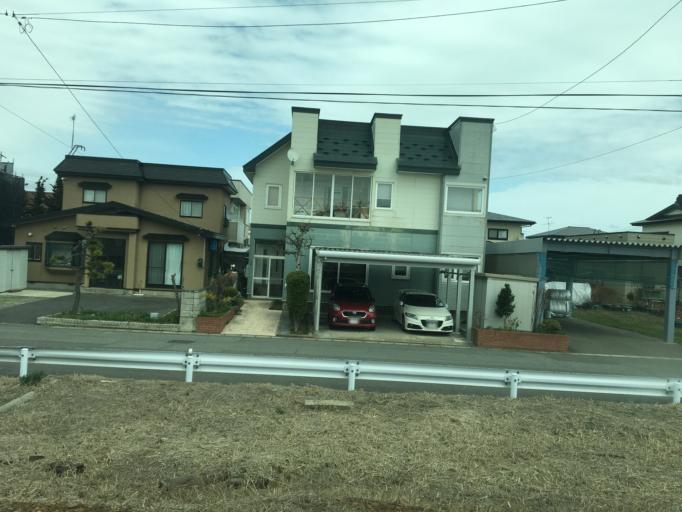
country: JP
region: Aomori
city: Hirosaki
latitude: 40.6539
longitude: 140.5001
